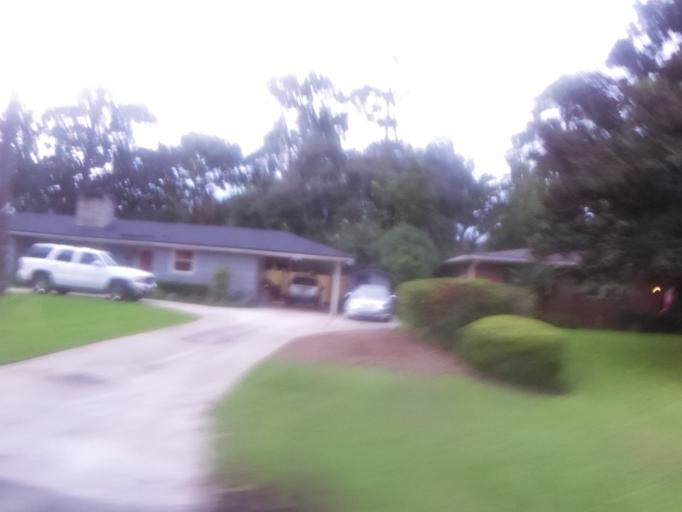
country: US
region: Florida
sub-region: Duval County
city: Jacksonville
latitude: 30.2765
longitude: -81.6993
